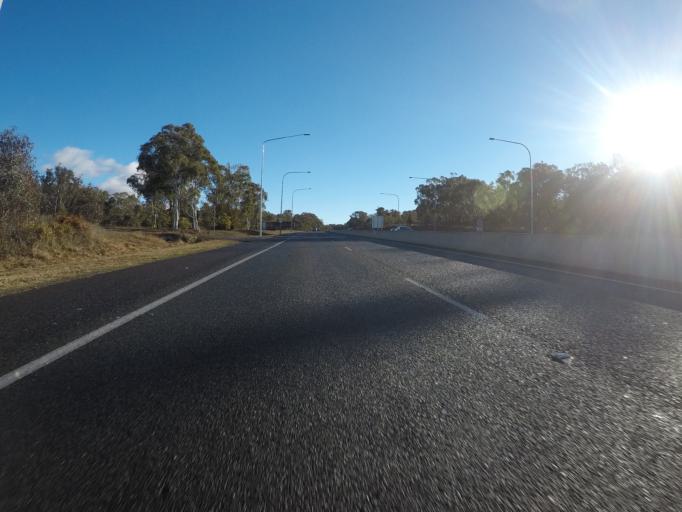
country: AU
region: Australian Capital Territory
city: Acton
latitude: -35.2784
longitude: 149.0866
